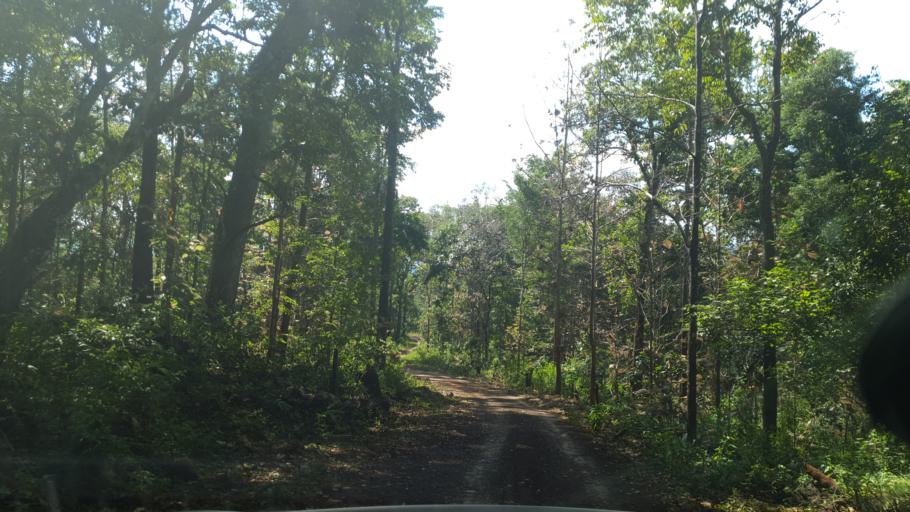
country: TH
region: Chiang Mai
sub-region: Amphoe Chiang Dao
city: Chiang Dao
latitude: 19.3007
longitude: 98.7172
